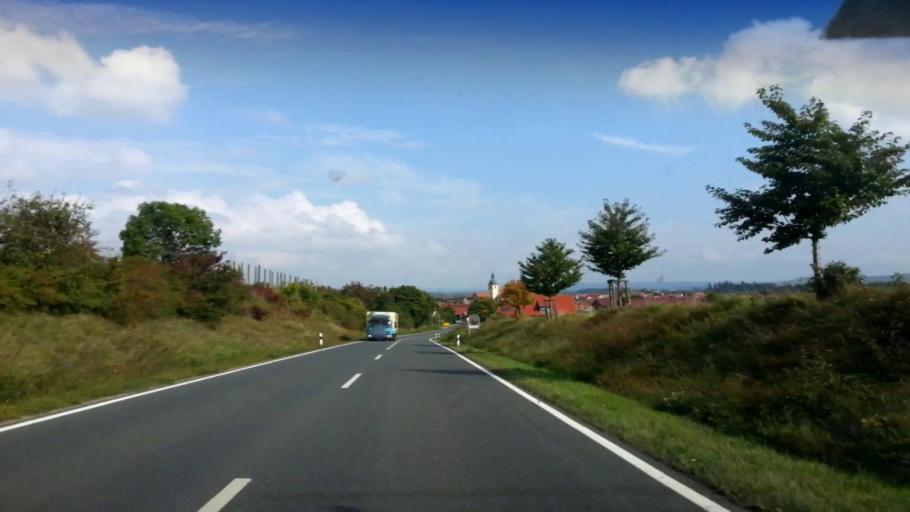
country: DE
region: Bavaria
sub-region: Regierungsbezirk Unterfranken
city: Wiesenbronn
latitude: 49.7446
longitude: 10.3013
